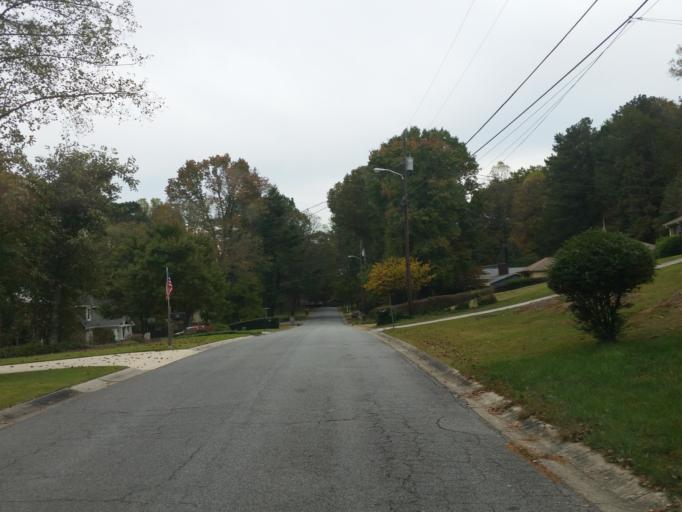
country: US
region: Georgia
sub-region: Cobb County
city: Marietta
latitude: 33.9520
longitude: -84.4714
